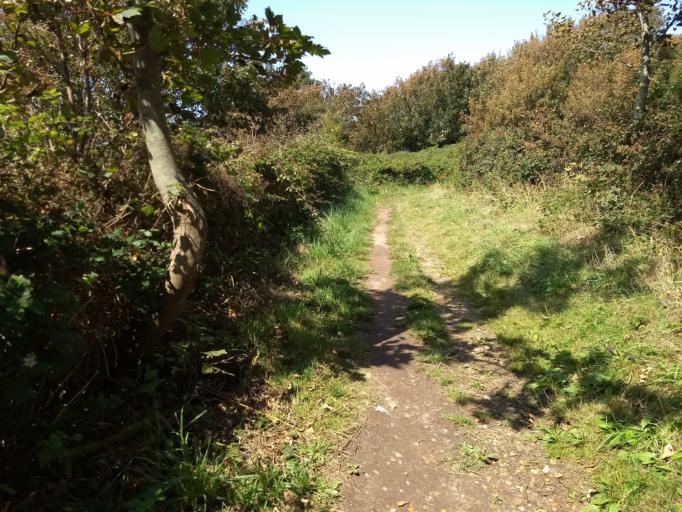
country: GB
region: England
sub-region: Isle of Wight
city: Totland
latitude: 50.6702
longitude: -1.5655
